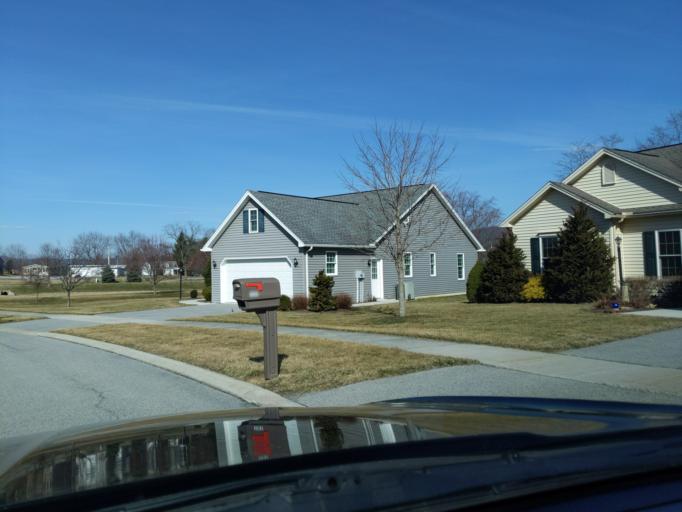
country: US
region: Pennsylvania
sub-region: Blair County
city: Martinsburg
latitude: 40.3051
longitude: -78.3233
